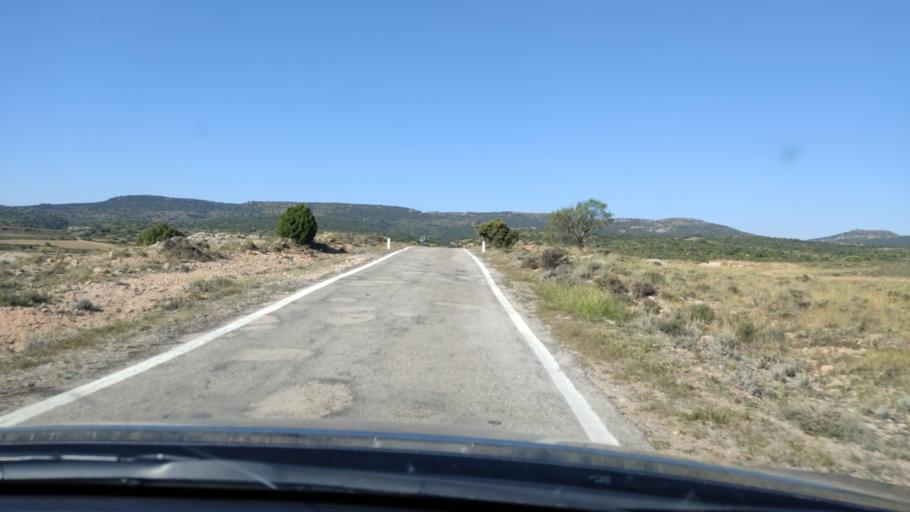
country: ES
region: Aragon
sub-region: Provincia de Teruel
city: Anadon
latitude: 41.0160
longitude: -0.9743
